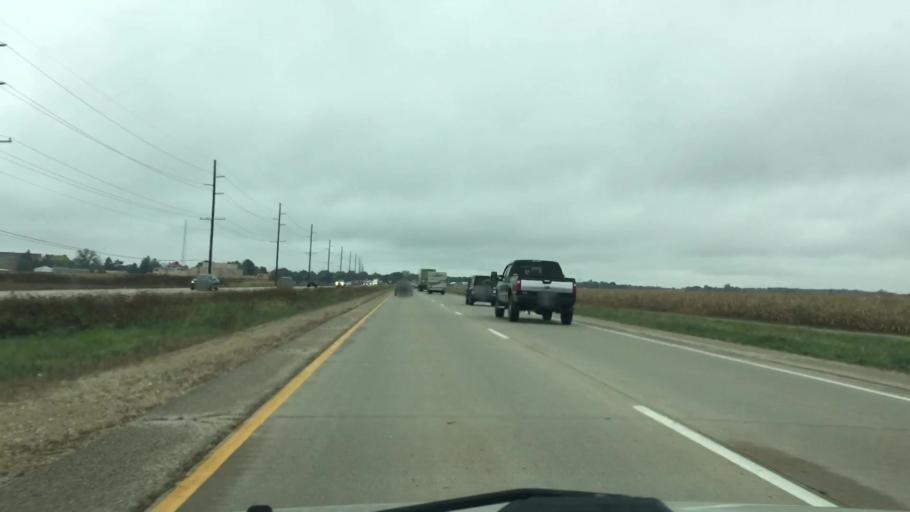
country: US
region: Wisconsin
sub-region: Rock County
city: Janesville
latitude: 42.7266
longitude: -89.0193
